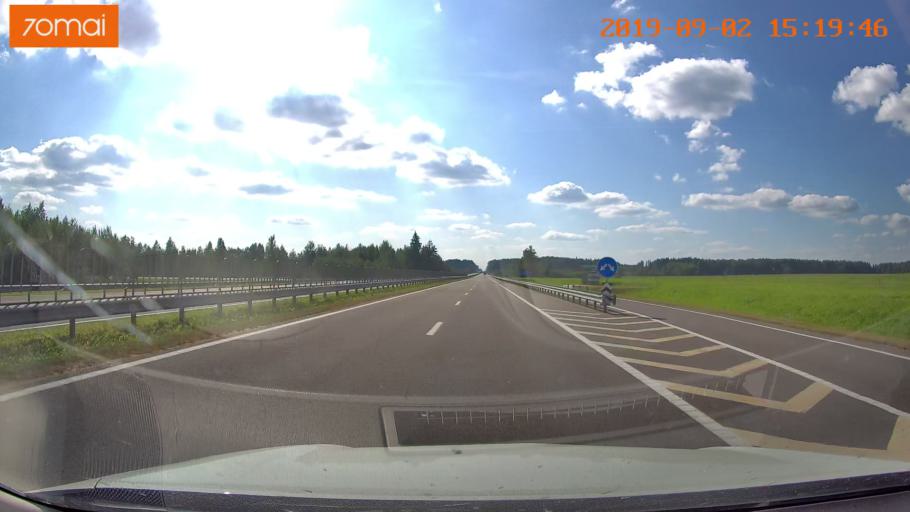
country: BY
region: Mogilev
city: Byalynichy
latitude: 53.9318
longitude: 29.5267
